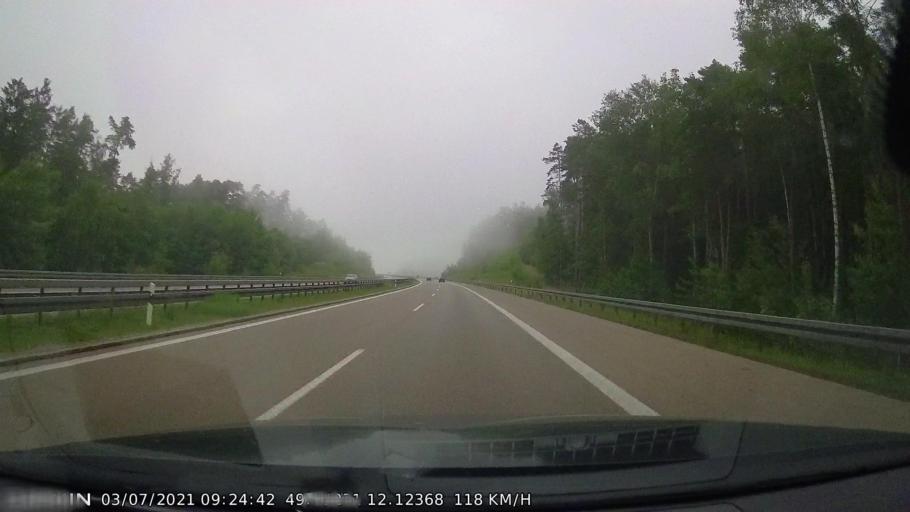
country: DE
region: Bavaria
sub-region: Upper Palatinate
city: Stulln
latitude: 49.4525
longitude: 12.1240
